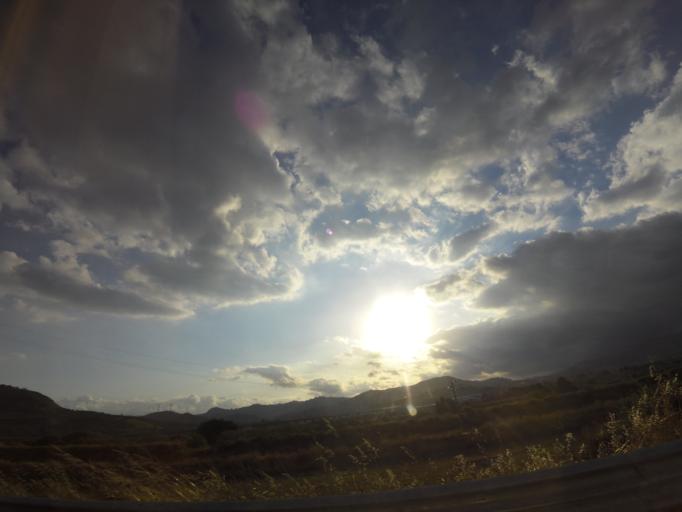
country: IT
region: Calabria
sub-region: Provincia di Catanzaro
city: Catanzaro
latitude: 38.8832
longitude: 16.5550
